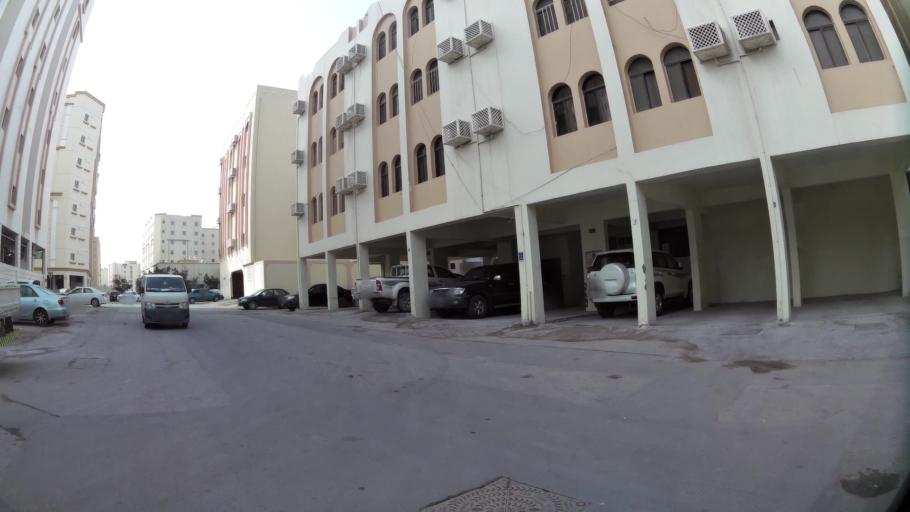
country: QA
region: Baladiyat ad Dawhah
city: Doha
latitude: 25.2797
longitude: 51.5454
